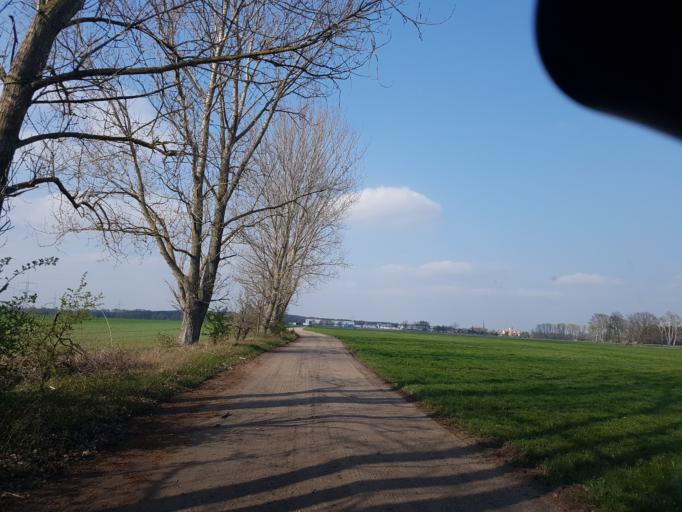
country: DE
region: Brandenburg
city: Ruckersdorf
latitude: 51.5957
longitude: 13.5322
